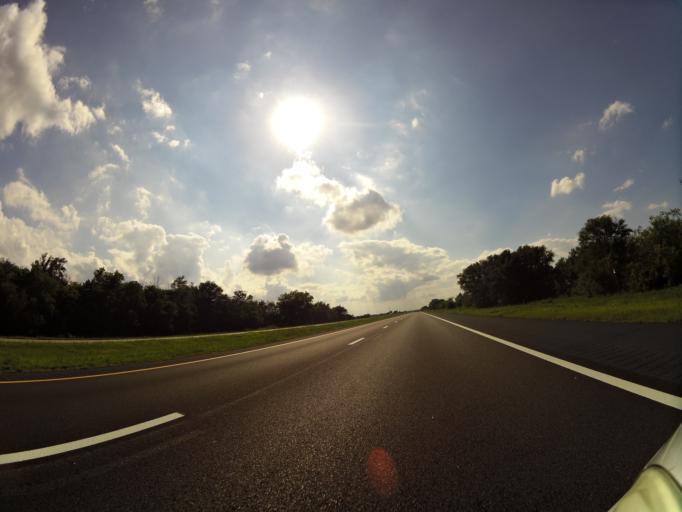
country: US
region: Kansas
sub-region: Reno County
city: Haven
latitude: 37.8856
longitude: -97.7335
